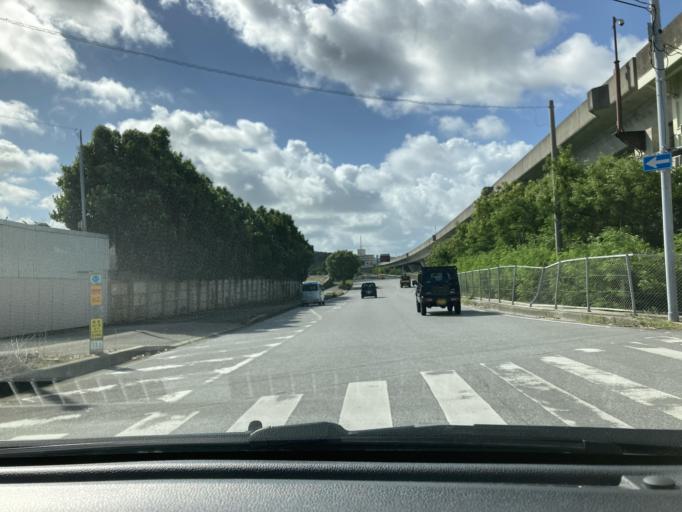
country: JP
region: Okinawa
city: Tomigusuku
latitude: 26.1808
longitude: 127.7243
